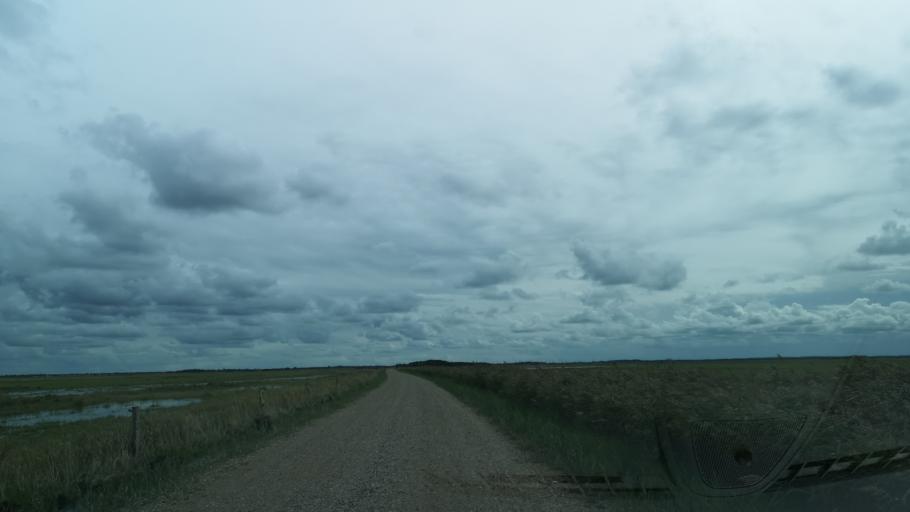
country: DK
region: Central Jutland
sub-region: Ringkobing-Skjern Kommune
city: Hvide Sande
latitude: 55.8676
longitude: 8.2309
